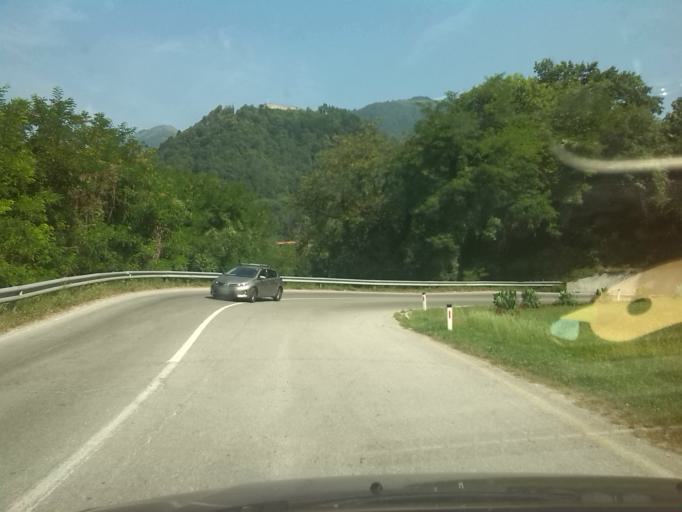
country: SI
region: Tolmin
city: Tolmin
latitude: 46.1825
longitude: 13.7302
